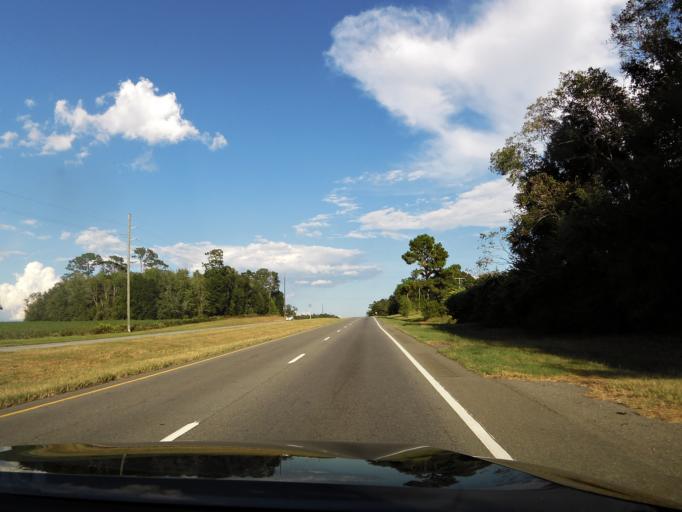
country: US
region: Georgia
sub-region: Brooks County
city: Quitman
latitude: 30.7889
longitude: -83.4989
